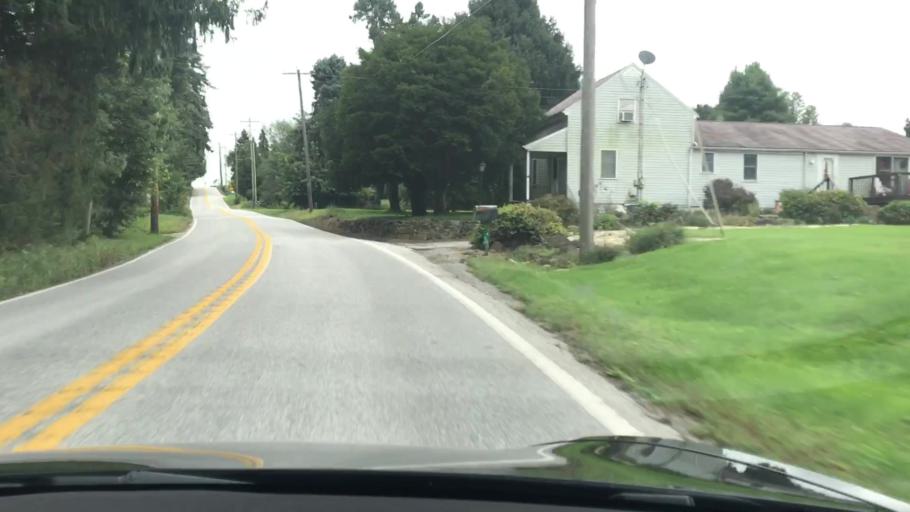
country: US
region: Pennsylvania
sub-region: York County
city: Dillsburg
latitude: 40.1392
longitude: -76.9642
